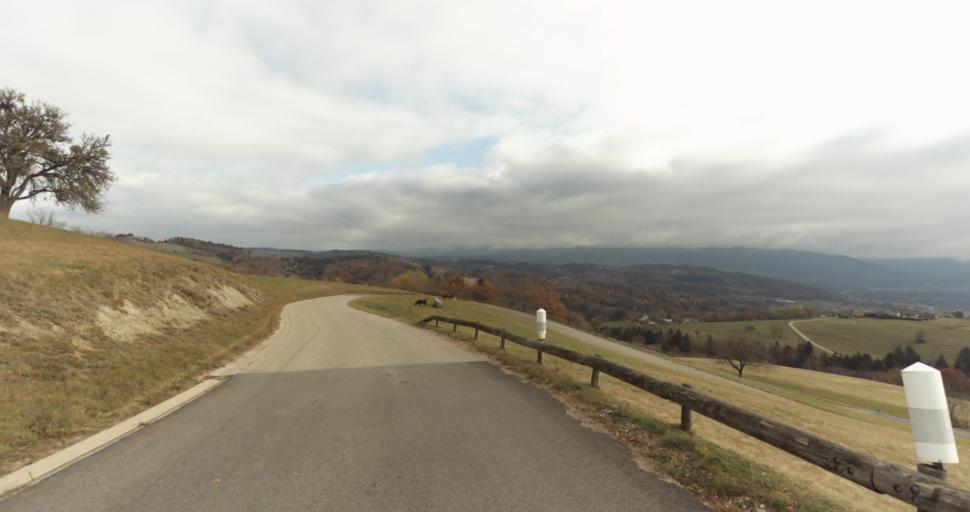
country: FR
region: Rhone-Alpes
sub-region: Departement de la Haute-Savoie
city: Epagny
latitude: 45.9647
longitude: 6.0903
